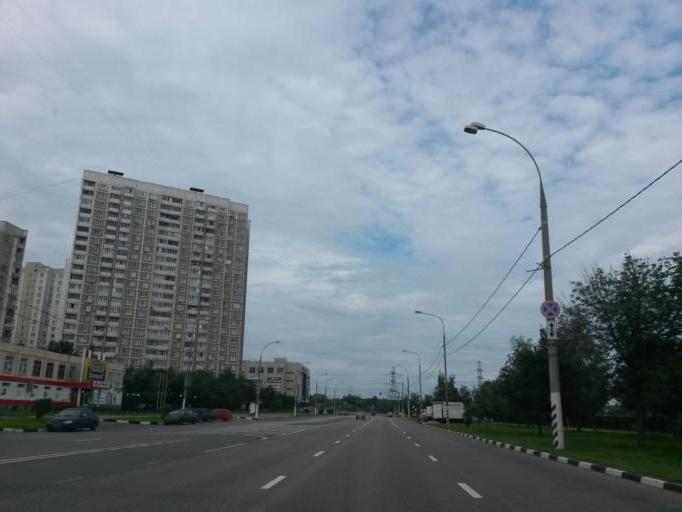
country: RU
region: Moscow
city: Chertanovo Yuzhnoye
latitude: 55.5735
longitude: 37.5705
